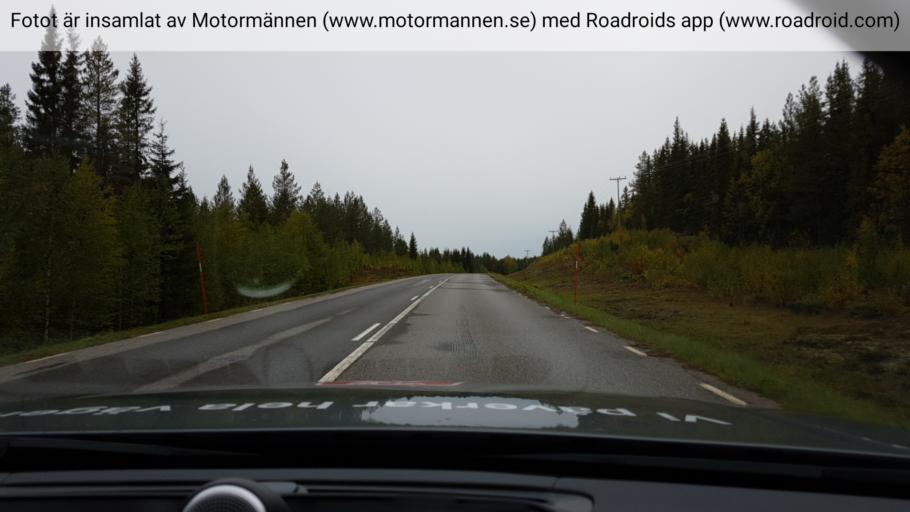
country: SE
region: Jaemtland
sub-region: Stroemsunds Kommun
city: Stroemsund
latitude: 64.2494
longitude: 15.4369
